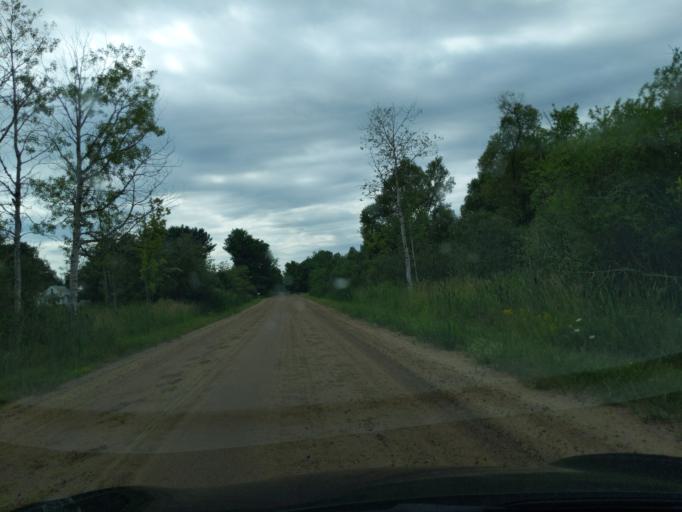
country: US
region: Michigan
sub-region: Clare County
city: Harrison
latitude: 44.0024
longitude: -84.9653
